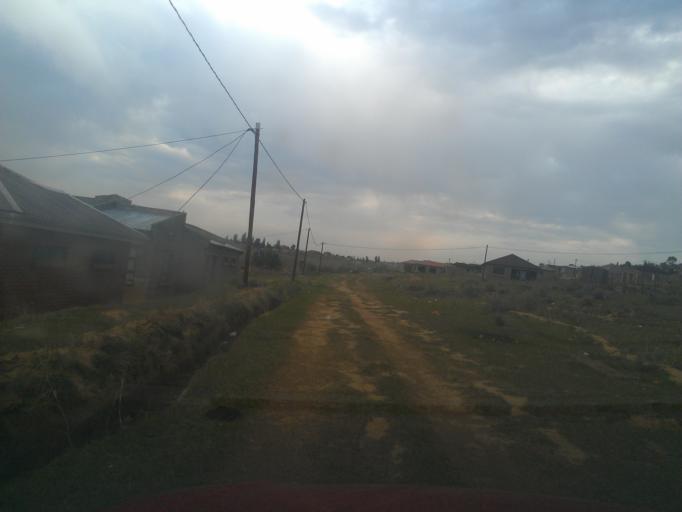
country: LS
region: Berea
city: Teyateyaneng
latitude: -29.1292
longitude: 27.7637
